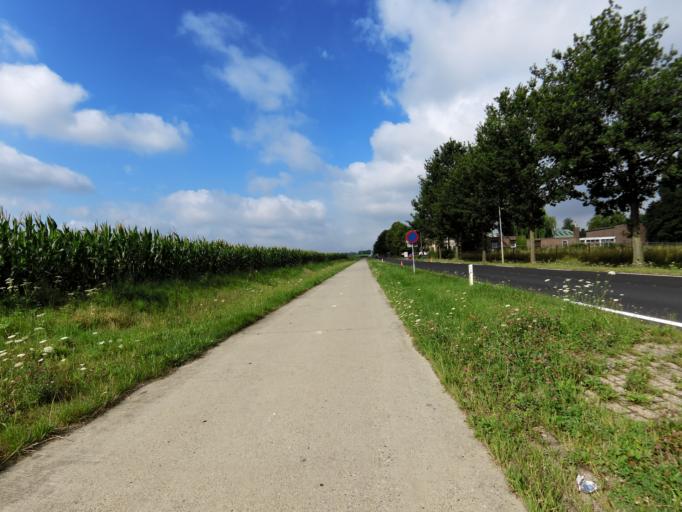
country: NL
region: Limburg
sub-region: Gemeente Nuth
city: Nuth
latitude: 50.9007
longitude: 5.8790
